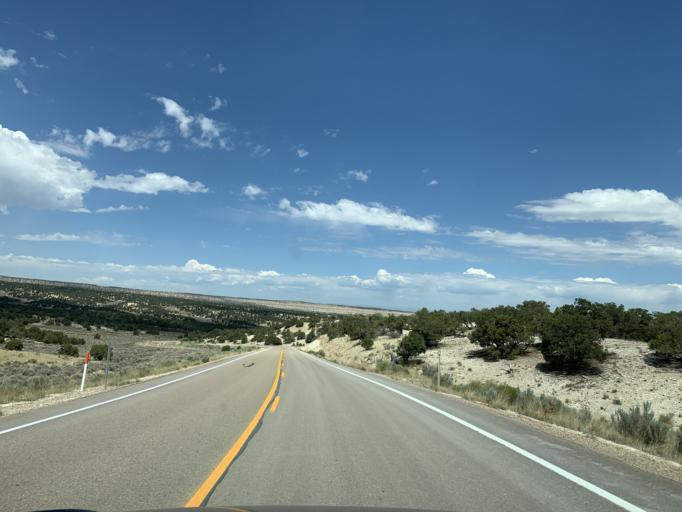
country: US
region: Utah
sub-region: Duchesne County
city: Duchesne
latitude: 39.8842
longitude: -110.2322
